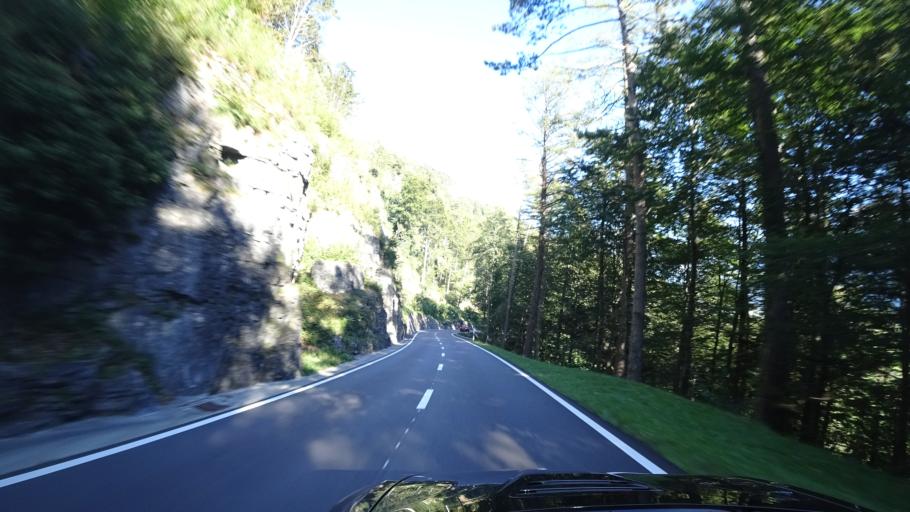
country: CH
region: Bern
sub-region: Interlaken-Oberhasli District
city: Meiringen
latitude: 46.7461
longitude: 8.1516
